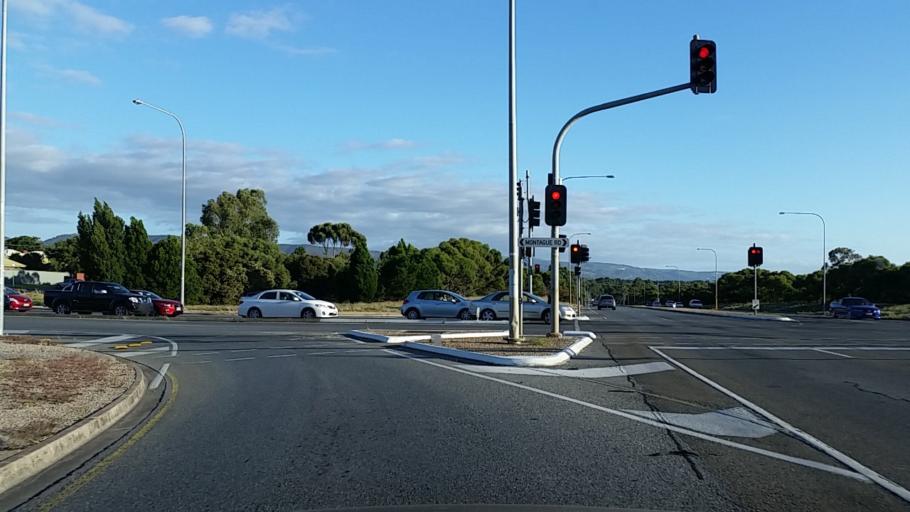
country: AU
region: South Australia
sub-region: Tea Tree Gully
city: Modbury
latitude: -34.8282
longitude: 138.6800
